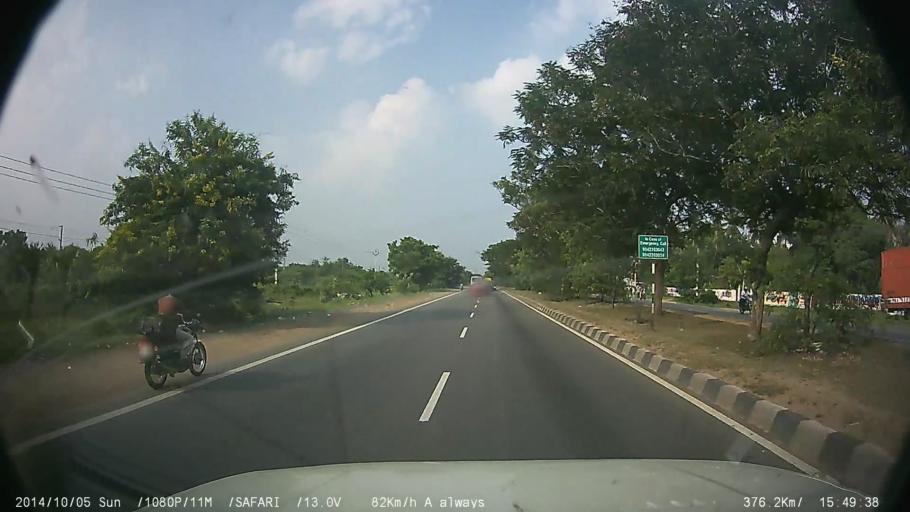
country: IN
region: Tamil Nadu
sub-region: Kancheepuram
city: Singapperumalkovil
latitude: 12.7731
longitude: 80.0086
